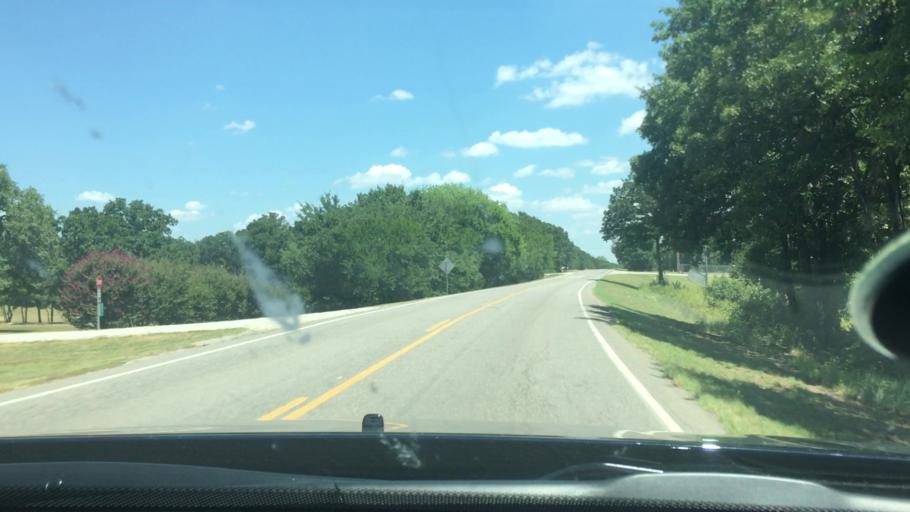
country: US
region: Oklahoma
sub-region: Carter County
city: Dickson
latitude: 34.1948
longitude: -96.9847
